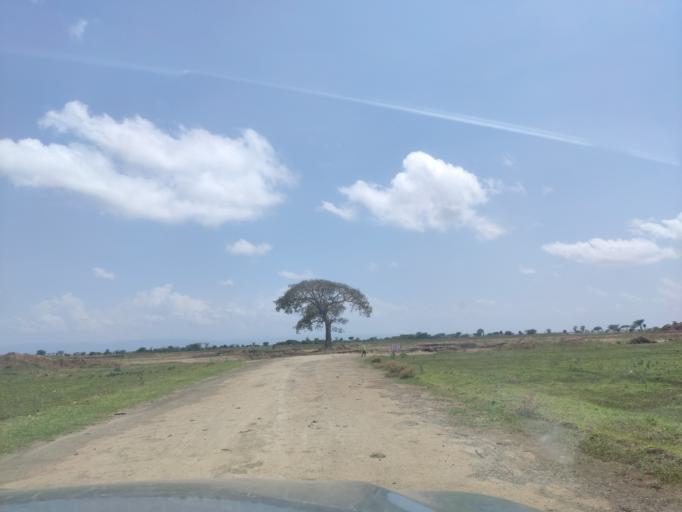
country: ET
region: Oromiya
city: Ziway
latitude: 8.2363
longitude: 38.8764
